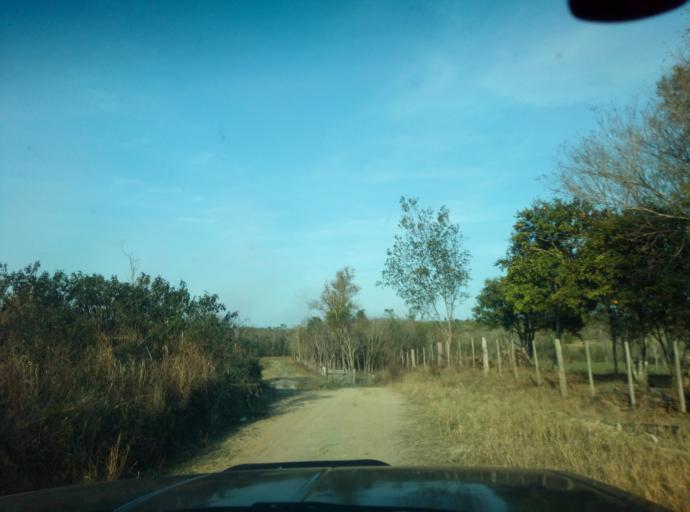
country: PY
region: Caaguazu
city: Yhu
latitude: -25.1991
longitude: -56.1140
